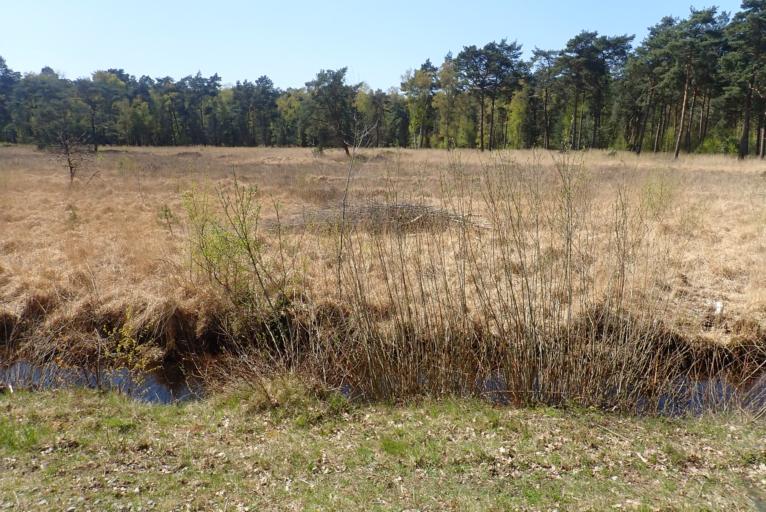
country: BE
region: Flanders
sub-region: Provincie Antwerpen
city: Kalmthout
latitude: 51.3544
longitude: 4.4916
